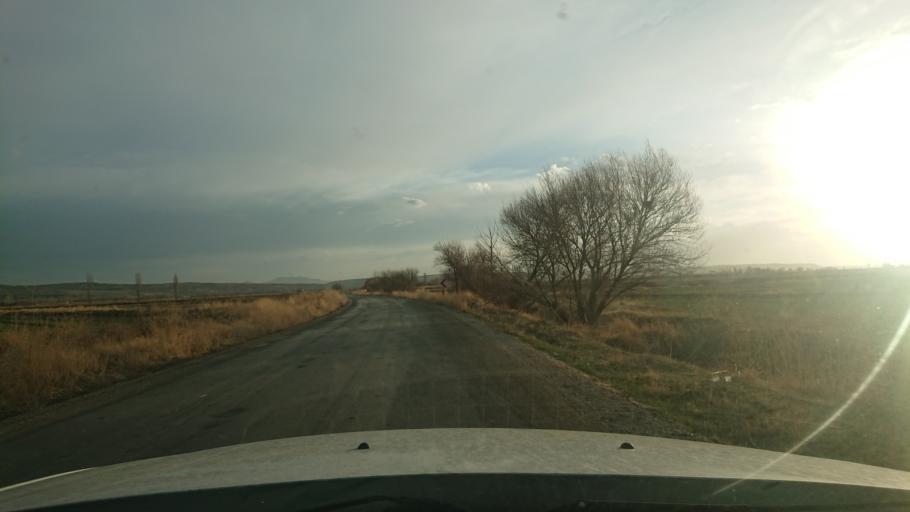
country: TR
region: Aksaray
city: Acipinar
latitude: 38.4754
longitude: 33.8628
